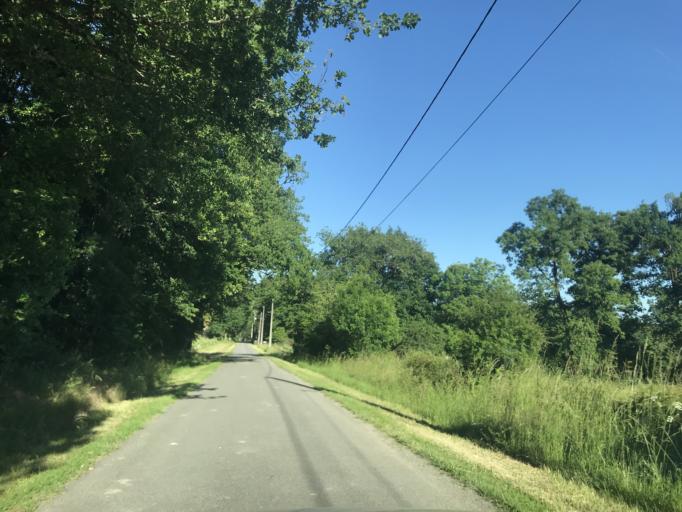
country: FR
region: Poitou-Charentes
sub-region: Departement de la Charente
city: Chalais
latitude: 45.2525
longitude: 0.0224
